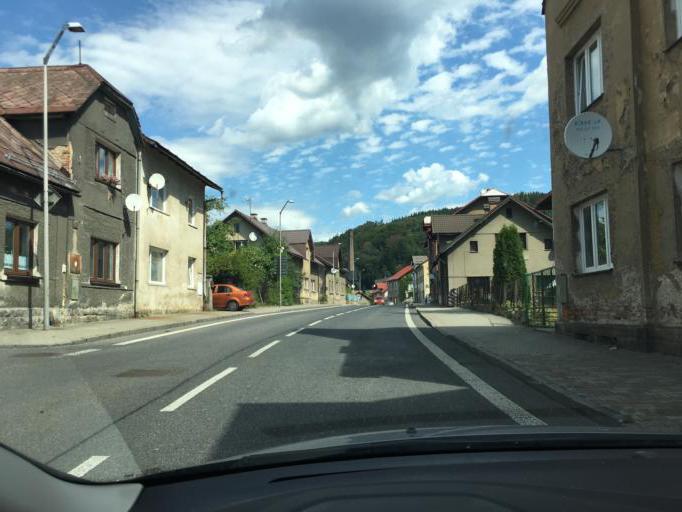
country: CZ
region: Liberecky
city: Velke Hamry
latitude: 50.7186
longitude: 15.3150
